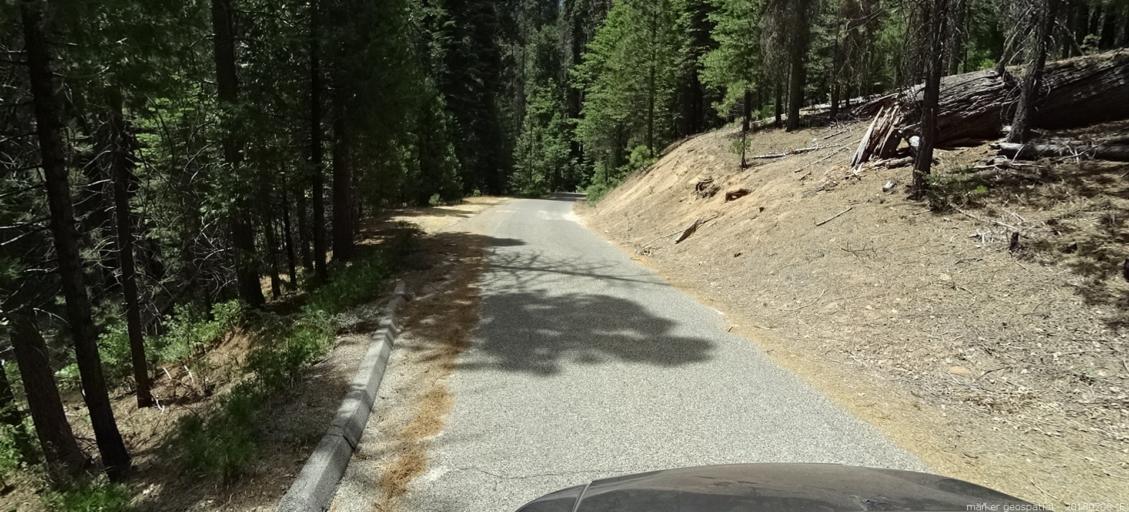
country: US
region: California
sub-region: Madera County
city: Oakhurst
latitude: 37.4091
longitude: -119.4022
